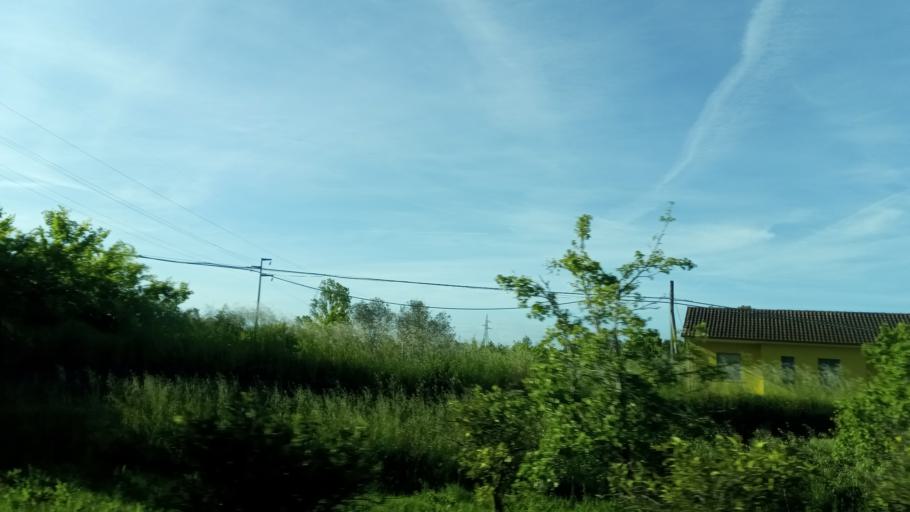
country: IT
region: Latium
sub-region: Provincia di Latina
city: Grunuovo-Campomaggiore San Luca
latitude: 41.2596
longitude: 13.7727
